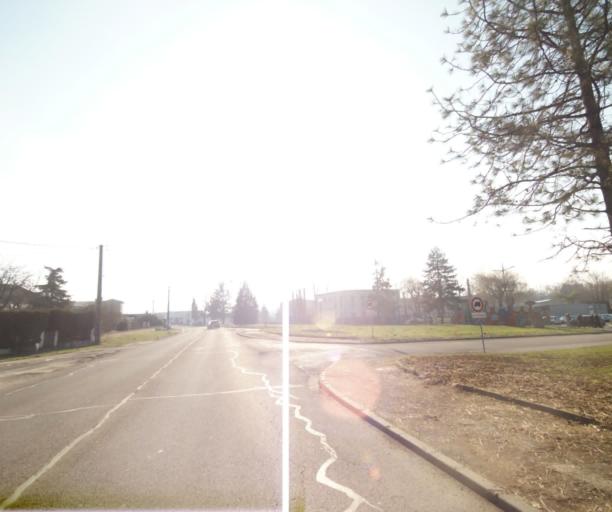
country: FR
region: Champagne-Ardenne
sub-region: Departement de la Haute-Marne
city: Wassy
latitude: 48.5047
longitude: 4.9432
